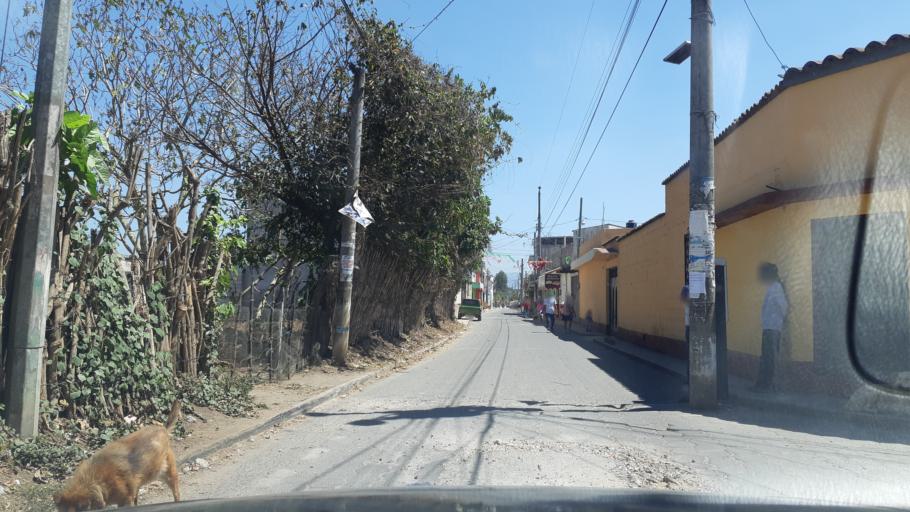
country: GT
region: Chimaltenango
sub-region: Municipio de Chimaltenango
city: Chimaltenango
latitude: 14.6519
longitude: -90.8125
